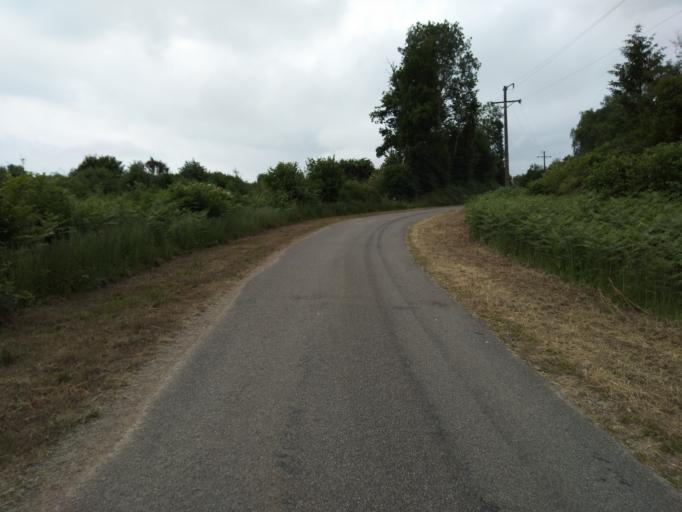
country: FR
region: Bourgogne
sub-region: Departement de la Cote-d'Or
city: Saulieu
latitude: 47.2869
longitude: 4.1297
